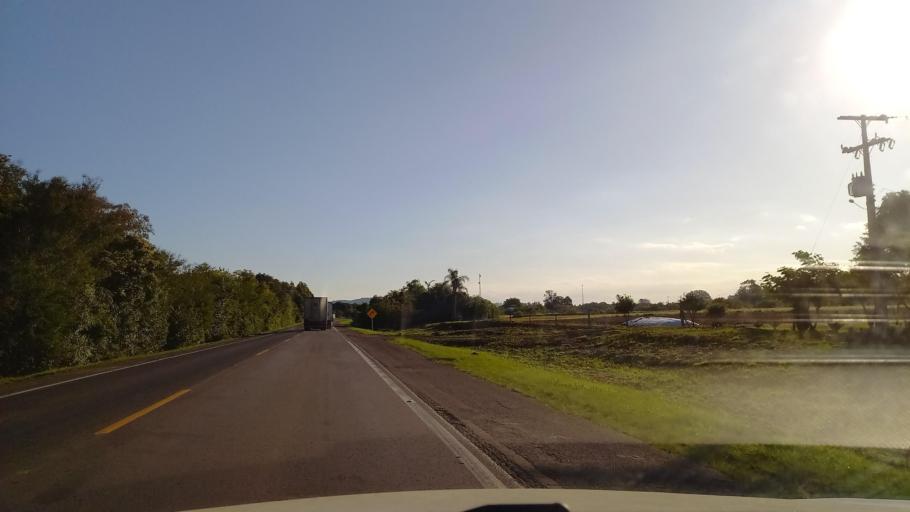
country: BR
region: Rio Grande do Sul
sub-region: Venancio Aires
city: Venancio Aires
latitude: -29.6687
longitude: -52.0333
